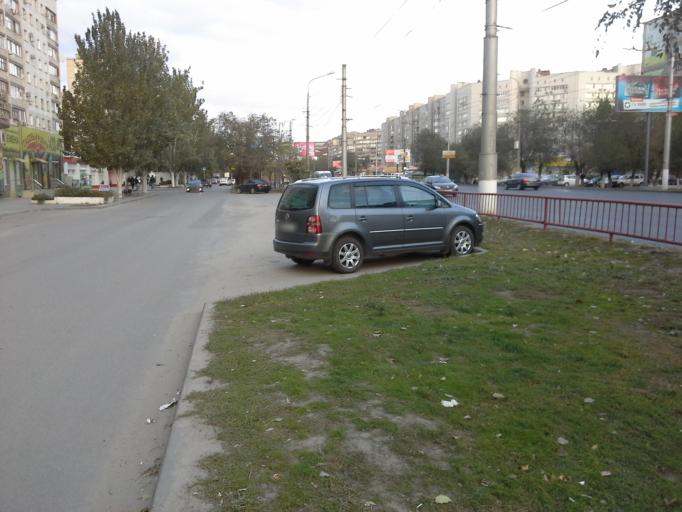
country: RU
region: Volgograd
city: Vodstroy
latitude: 48.8166
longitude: 44.6258
